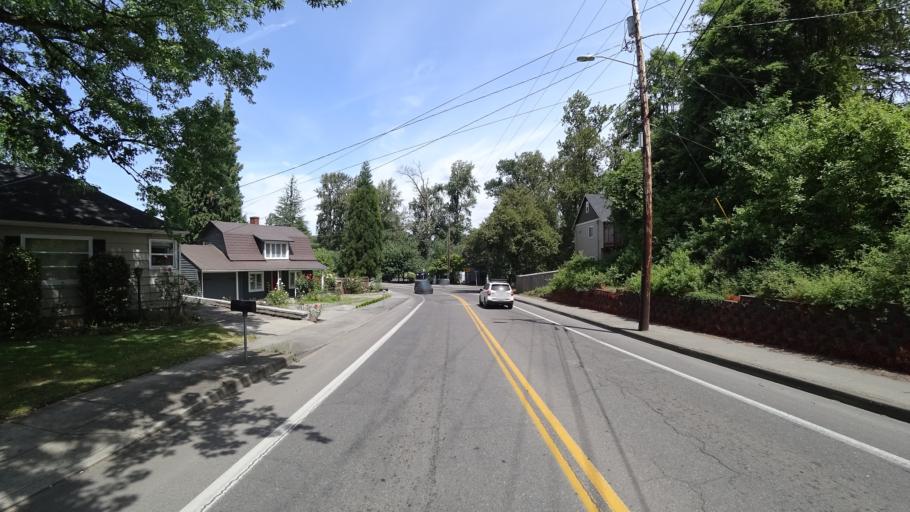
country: US
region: Oregon
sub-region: Clackamas County
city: Milwaukie
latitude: 45.4602
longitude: -122.6177
